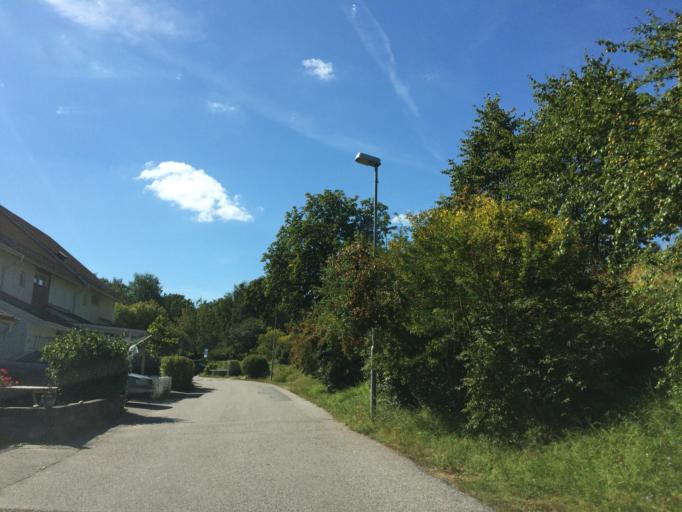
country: SE
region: Stockholm
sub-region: Sollentuna Kommun
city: Sollentuna
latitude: 59.4582
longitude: 17.9107
